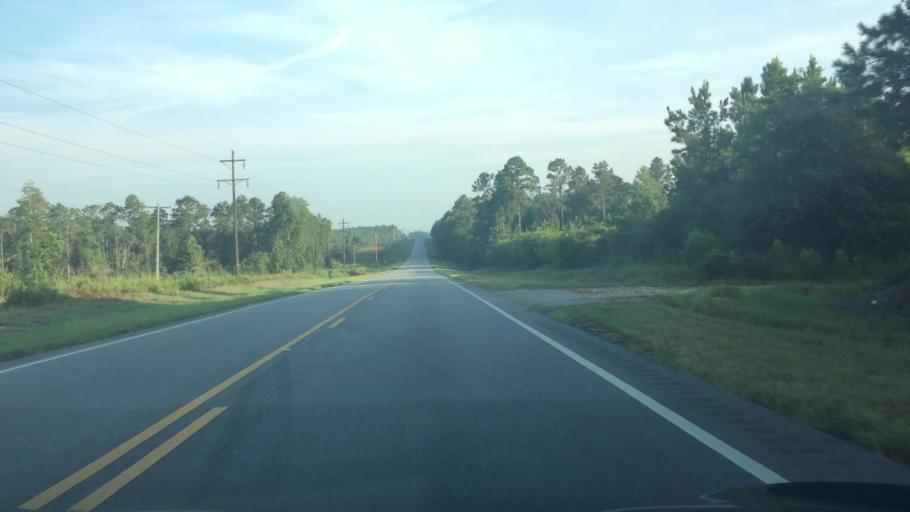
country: US
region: Alabama
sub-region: Covington County
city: Florala
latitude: 31.0342
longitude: -86.3745
